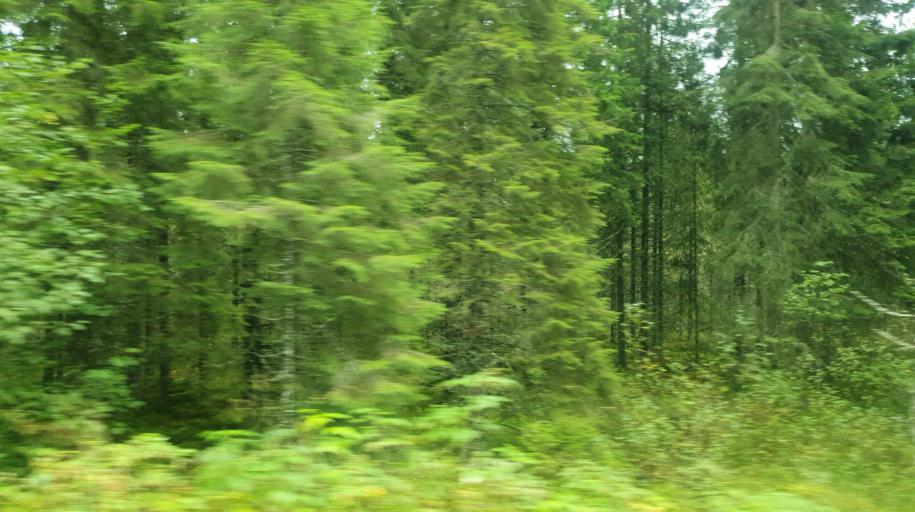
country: NO
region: Nord-Trondelag
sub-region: Levanger
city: Skogn
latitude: 63.6178
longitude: 11.2190
